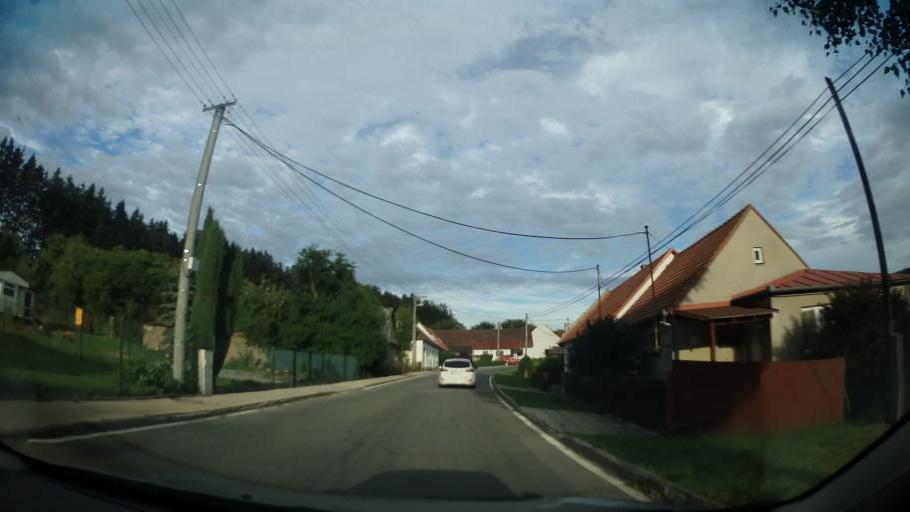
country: CZ
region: Olomoucky
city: Horni Stepanov
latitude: 49.5614
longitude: 16.7563
